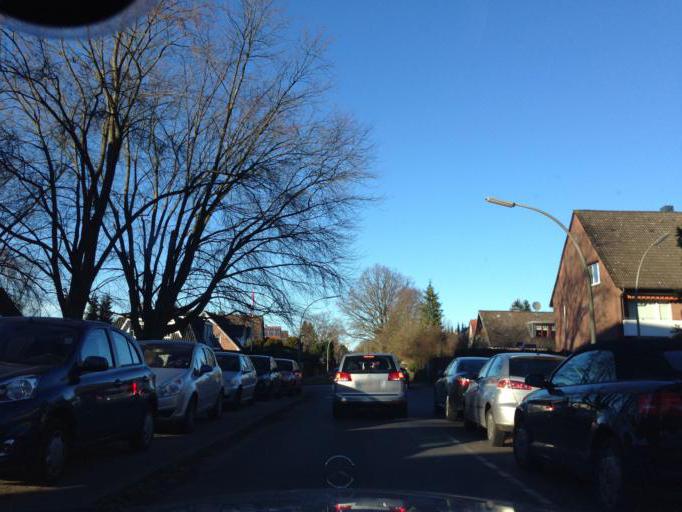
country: DE
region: Hamburg
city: Farmsen-Berne
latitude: 53.6066
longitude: 10.1289
